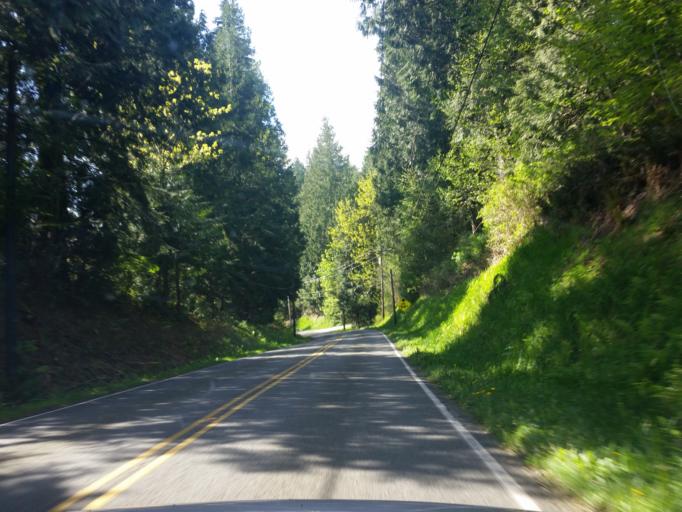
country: US
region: Washington
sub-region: Snohomish County
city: Three Lakes
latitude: 47.9629
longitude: -121.9347
